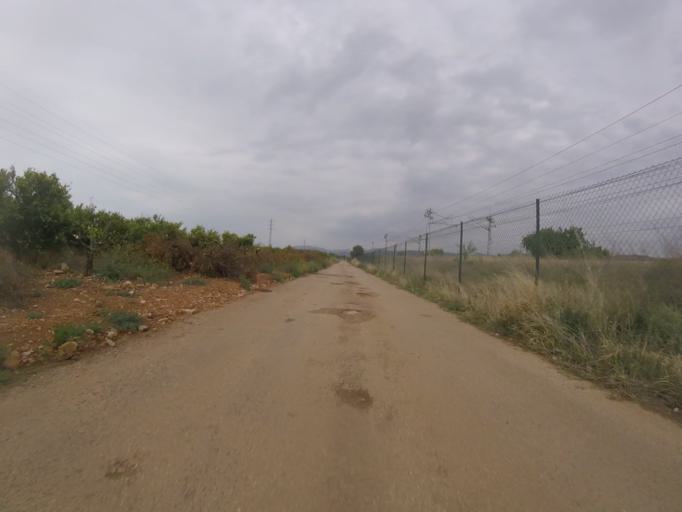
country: ES
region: Valencia
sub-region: Provincia de Castello
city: Torreblanca
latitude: 40.2173
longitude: 0.2048
